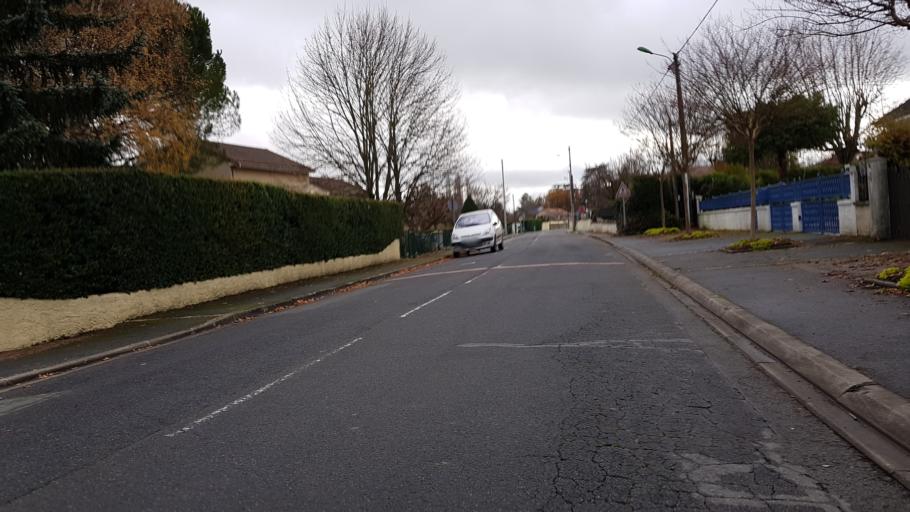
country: FR
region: Poitou-Charentes
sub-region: Departement de la Vienne
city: Chasseneuil-du-Poitou
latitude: 46.6560
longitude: 0.3803
